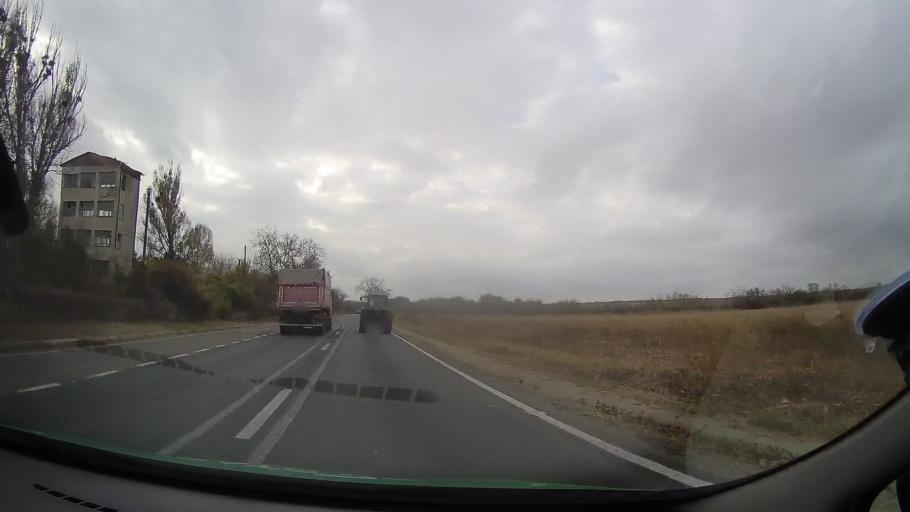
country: RO
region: Constanta
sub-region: Municipiul Medgidia
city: Medgidia
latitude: 44.2677
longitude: 28.2640
